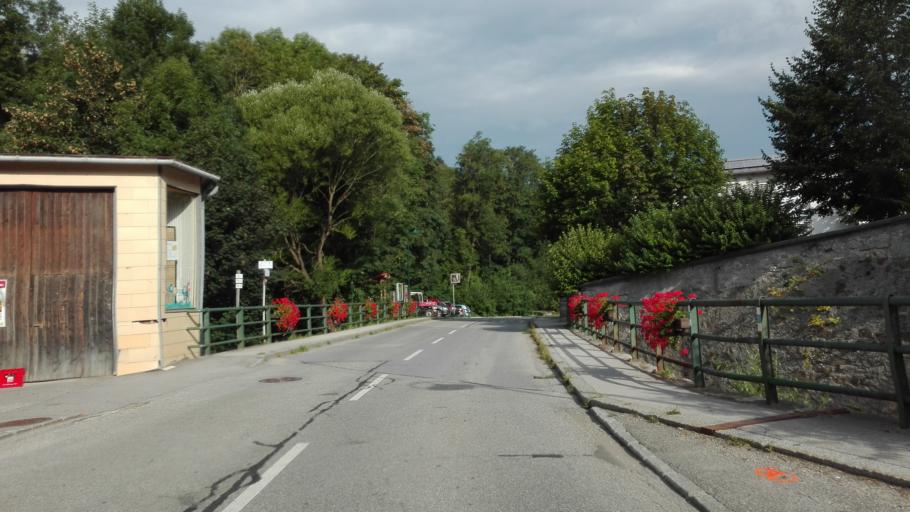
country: AT
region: Lower Austria
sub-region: Politischer Bezirk Sankt Polten
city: Stossing
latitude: 48.1228
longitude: 15.8138
